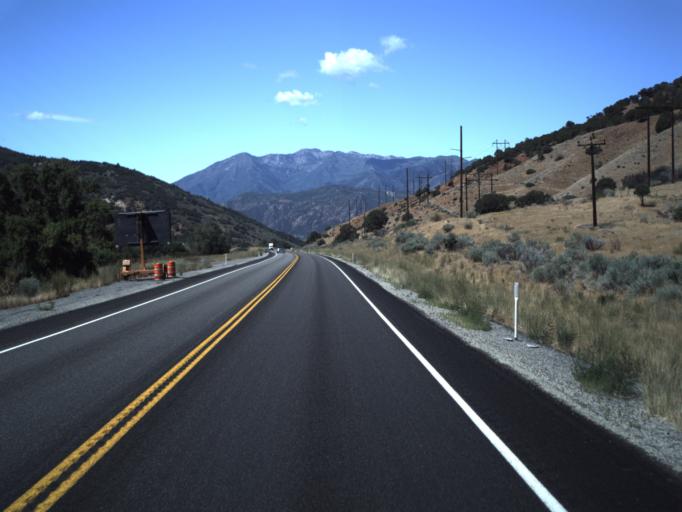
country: US
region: Utah
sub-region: Utah County
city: Mapleton
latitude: 39.9971
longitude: -111.4226
